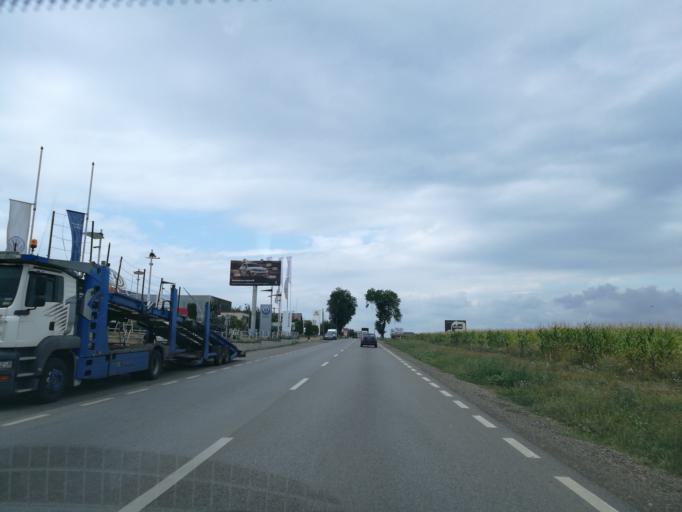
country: RO
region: Suceava
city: Suceava
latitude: 47.6226
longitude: 26.2388
